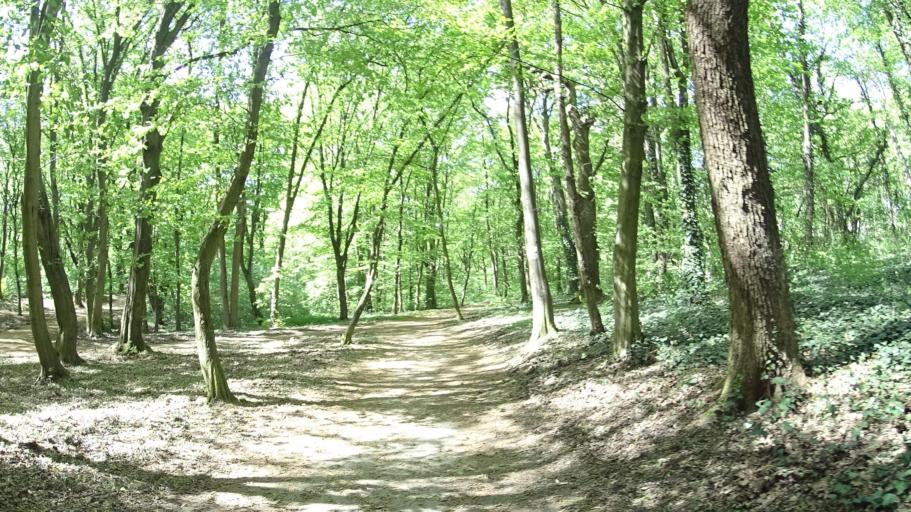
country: HU
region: Pest
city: Godollo
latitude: 47.5979
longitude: 19.3328
